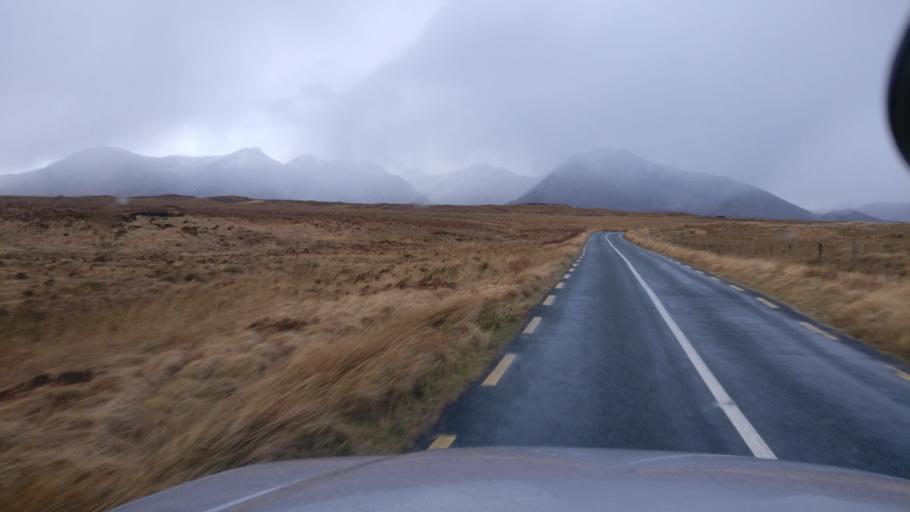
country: IE
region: Connaught
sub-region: County Galway
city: Clifden
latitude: 53.4397
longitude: -9.7708
